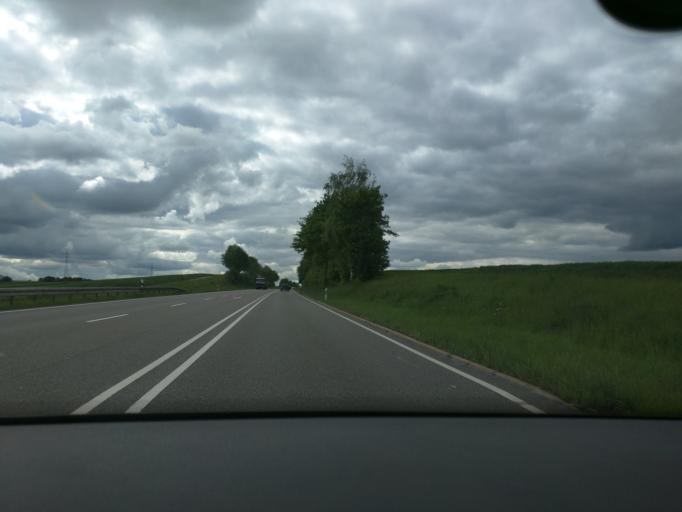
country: DE
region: Baden-Wuerttemberg
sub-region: Regierungsbezirk Stuttgart
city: Bondorf
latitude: 48.4984
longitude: 8.8676
